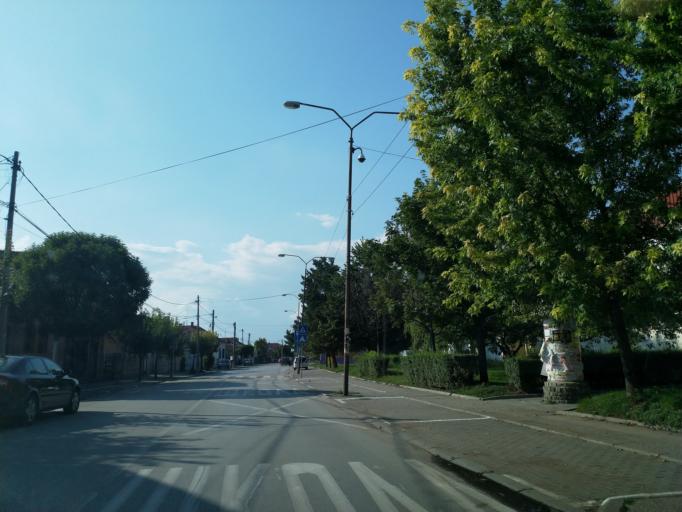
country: RS
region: Central Serbia
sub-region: Pomoravski Okrug
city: Paracin
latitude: 43.8606
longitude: 21.4067
